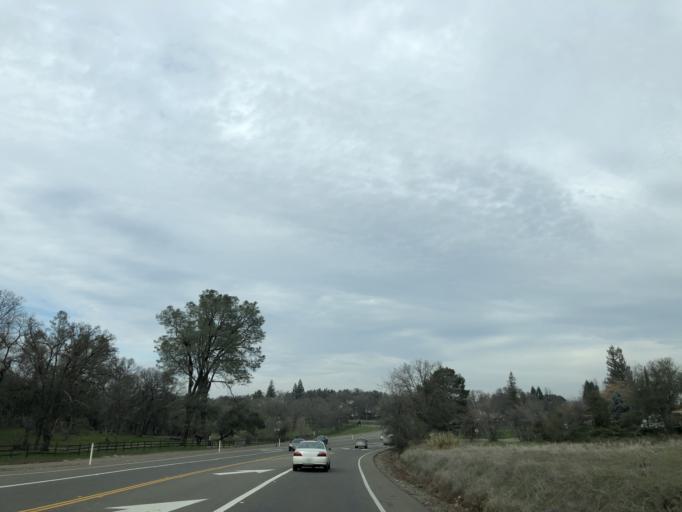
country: US
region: California
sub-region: El Dorado County
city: El Dorado Hills
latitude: 38.6999
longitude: -121.0834
